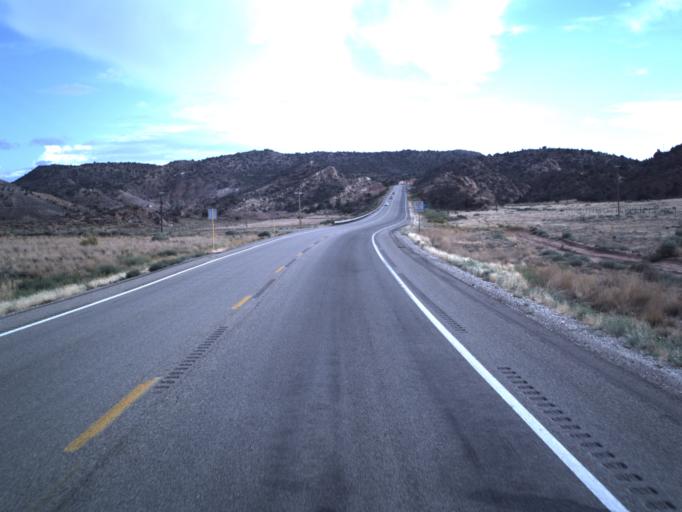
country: US
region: Utah
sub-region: Grand County
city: Moab
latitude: 38.4371
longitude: -109.4286
